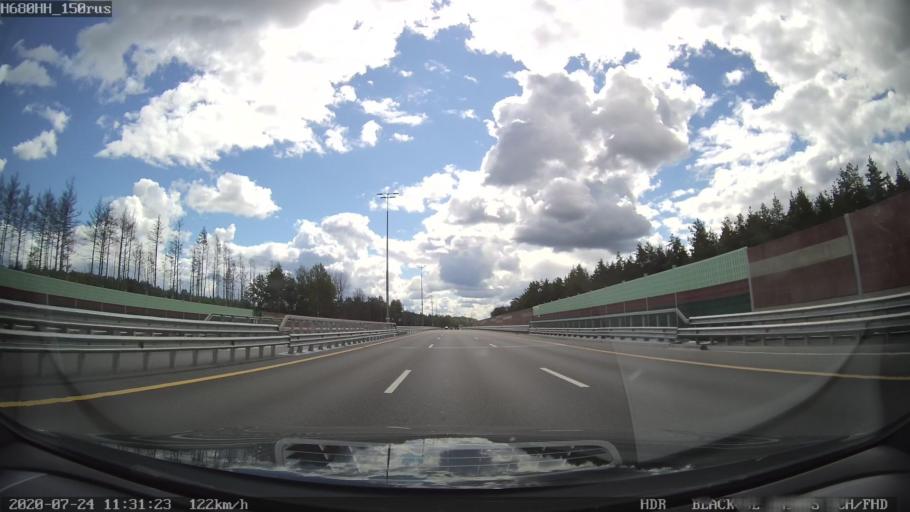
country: RU
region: Leningrad
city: Krasnyy Bor
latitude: 59.6571
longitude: 30.6357
